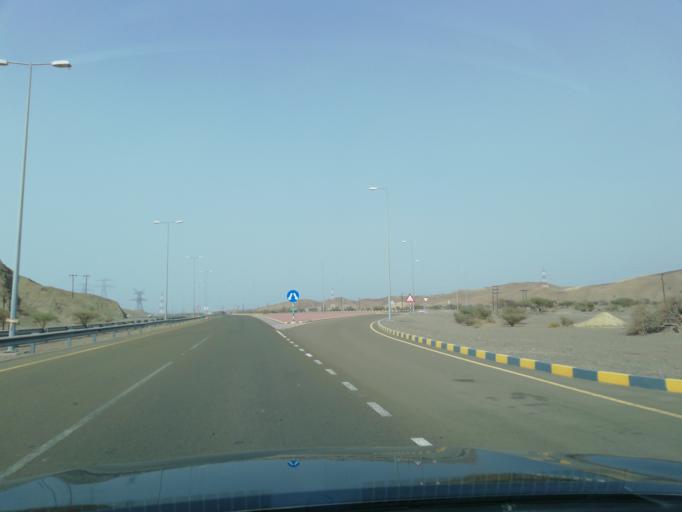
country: OM
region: Al Batinah
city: Al Liwa'
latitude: 24.3483
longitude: 56.5176
